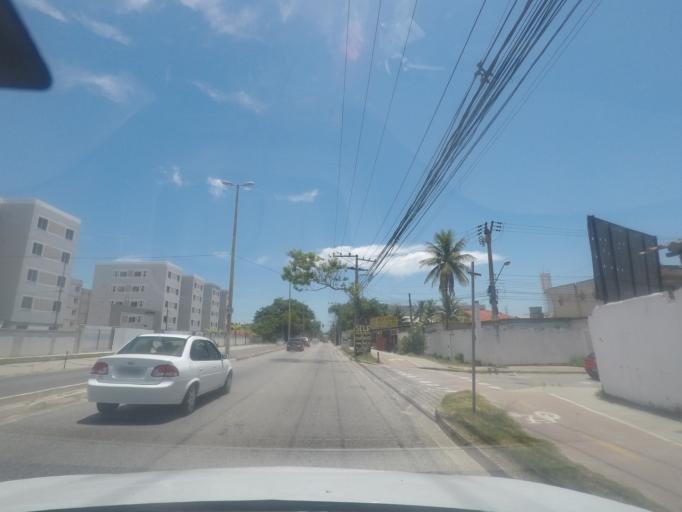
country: BR
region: Rio de Janeiro
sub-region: Itaguai
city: Itaguai
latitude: -22.8978
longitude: -43.6783
